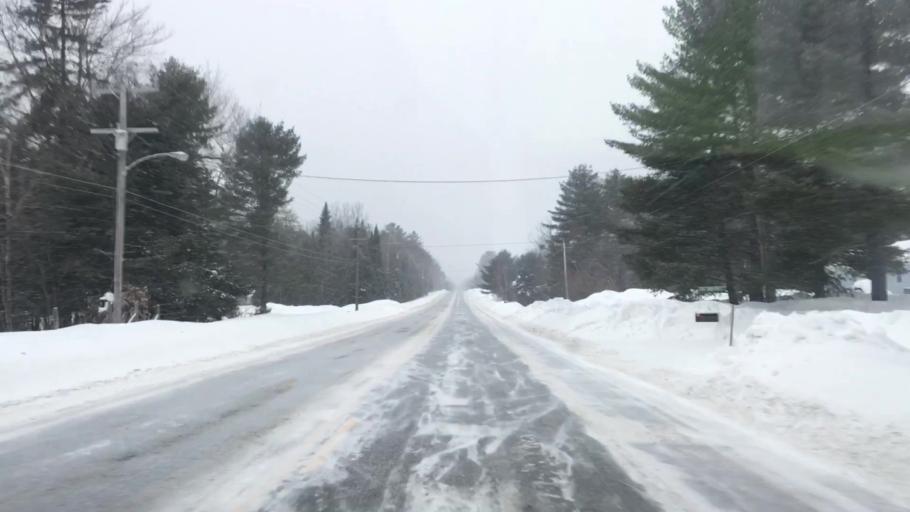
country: US
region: Maine
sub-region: Penobscot County
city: Medway
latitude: 45.5458
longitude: -68.3732
